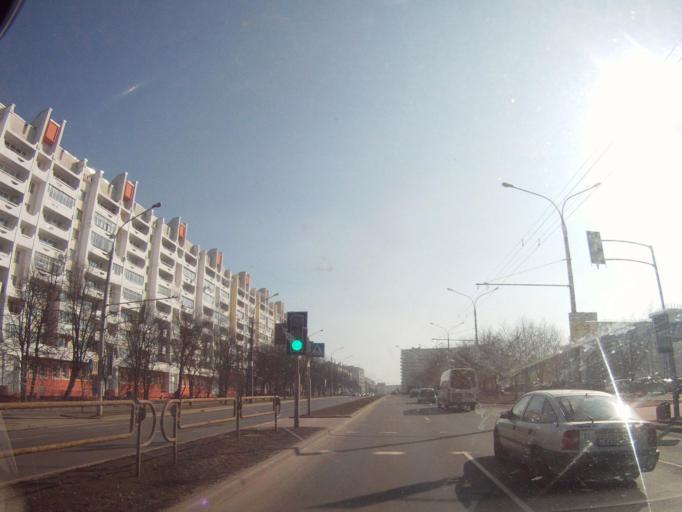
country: BY
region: Minsk
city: Minsk
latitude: 53.9275
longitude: 27.5890
